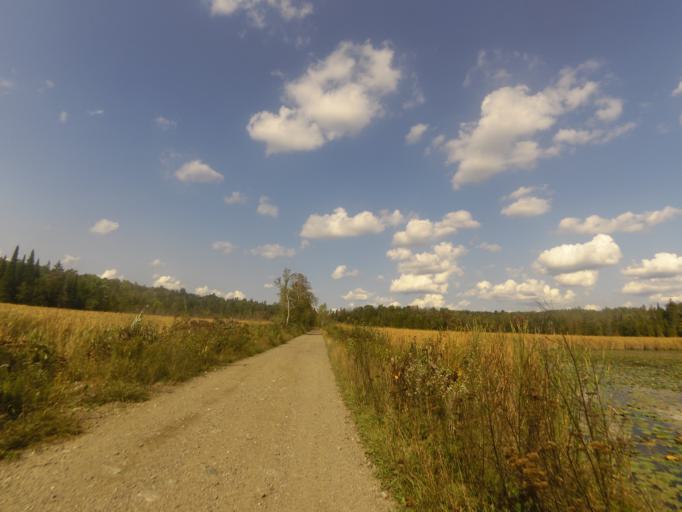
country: CA
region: Ontario
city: Renfrew
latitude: 45.1348
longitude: -76.6865
